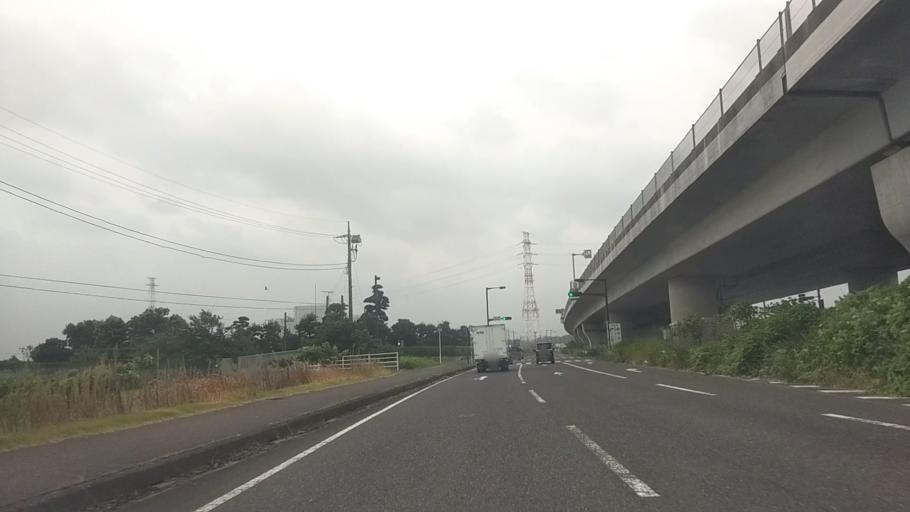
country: JP
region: Chiba
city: Kisarazu
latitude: 35.4033
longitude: 139.9661
